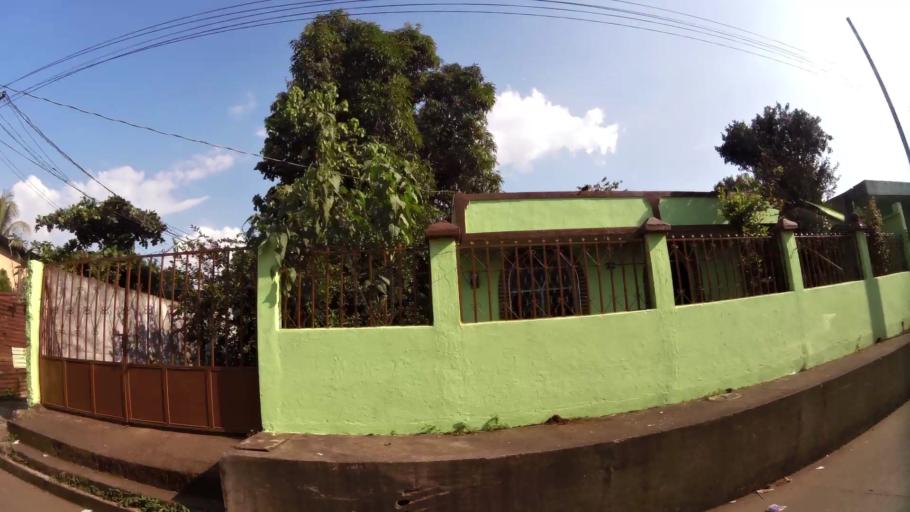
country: GT
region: Retalhuleu
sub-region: Municipio de Retalhuleu
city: Retalhuleu
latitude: 14.5364
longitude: -91.6927
